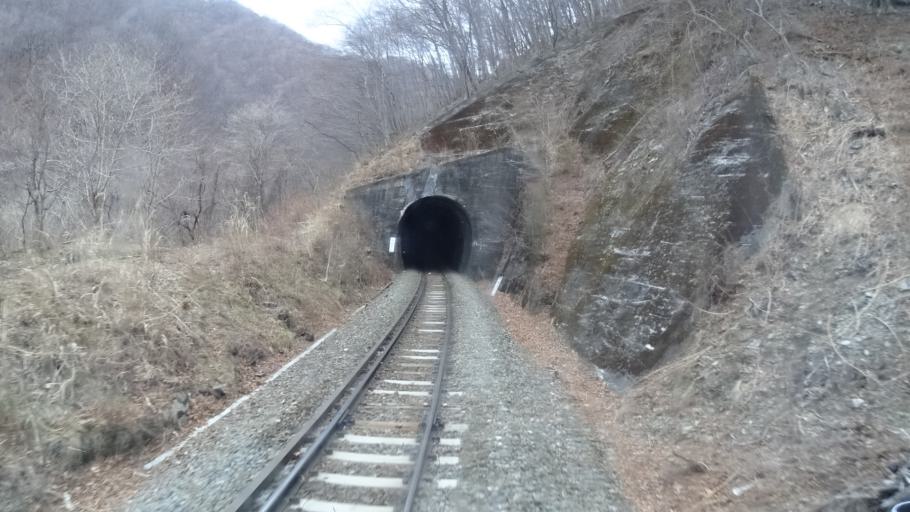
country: JP
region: Iwate
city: Tono
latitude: 39.2430
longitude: 141.6707
